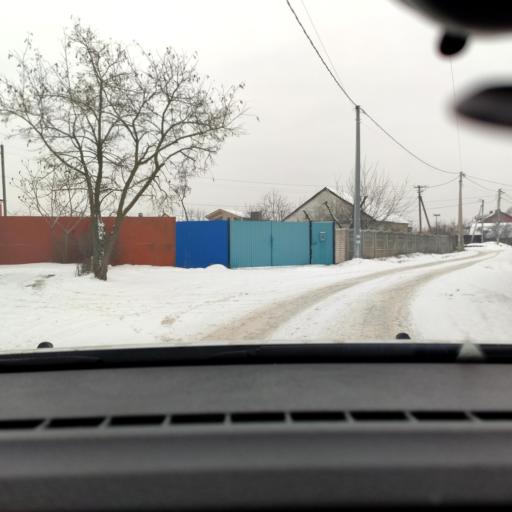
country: RU
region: Voronezj
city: Podgornoye
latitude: 51.7957
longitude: 39.1405
